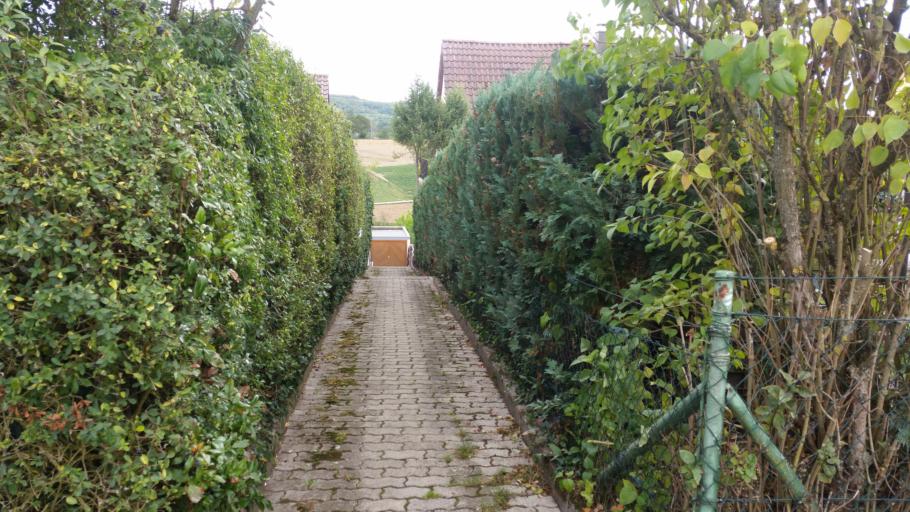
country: DE
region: Baden-Wuerttemberg
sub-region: Regierungsbezirk Stuttgart
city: Leonberg
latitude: 48.7987
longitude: 8.9924
